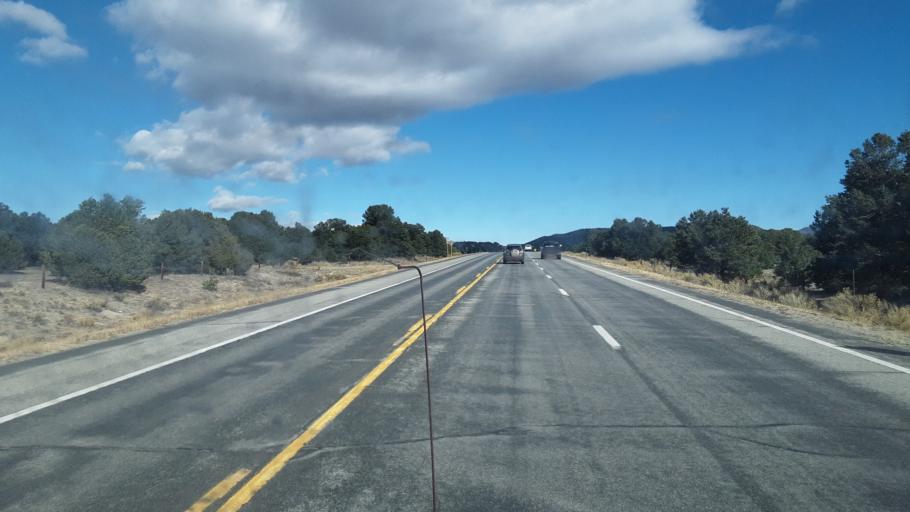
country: US
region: Colorado
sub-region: Chaffee County
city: Salida
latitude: 38.6010
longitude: -106.0832
